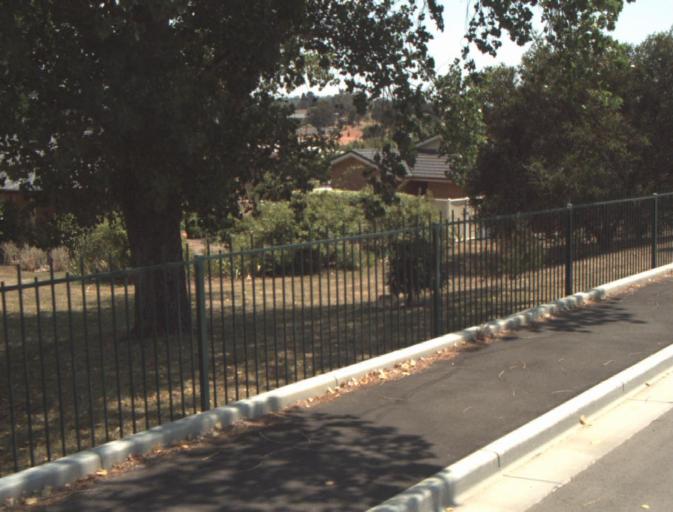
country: AU
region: Tasmania
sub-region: Launceston
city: Summerhill
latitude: -41.4874
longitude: 147.1678
